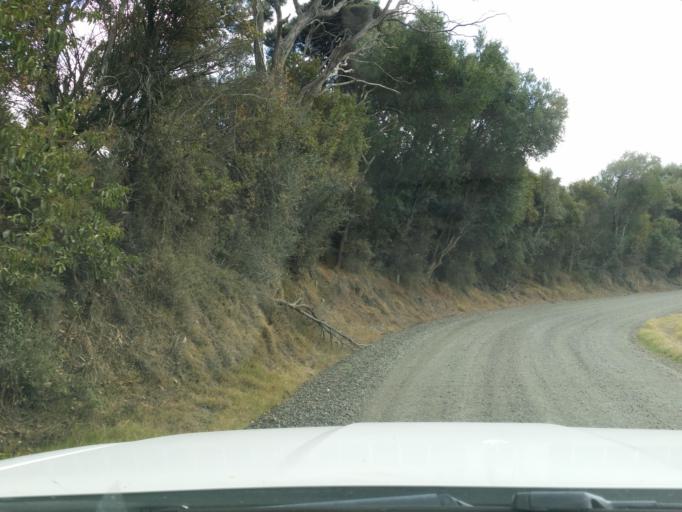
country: NZ
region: Auckland
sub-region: Auckland
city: Wellsford
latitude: -36.3627
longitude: 174.1777
